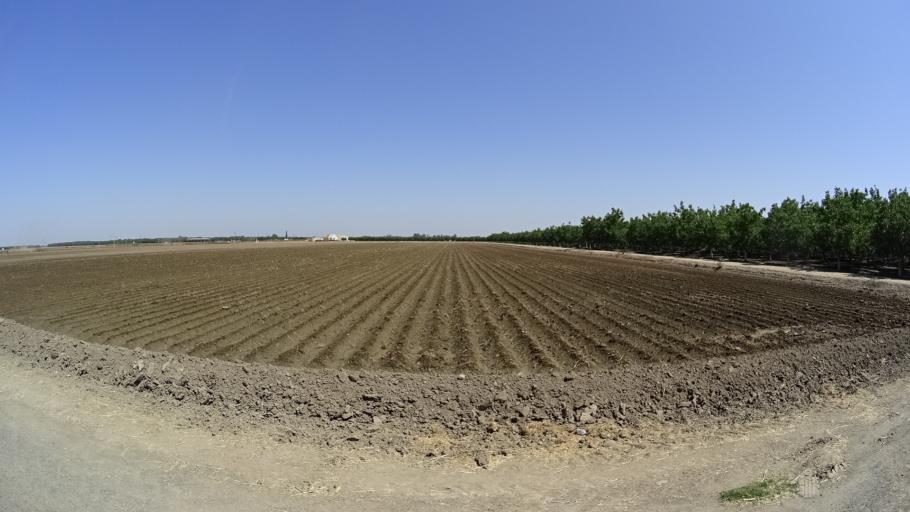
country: US
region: California
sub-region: Kings County
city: Lucerne
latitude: 36.3717
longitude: -119.6957
